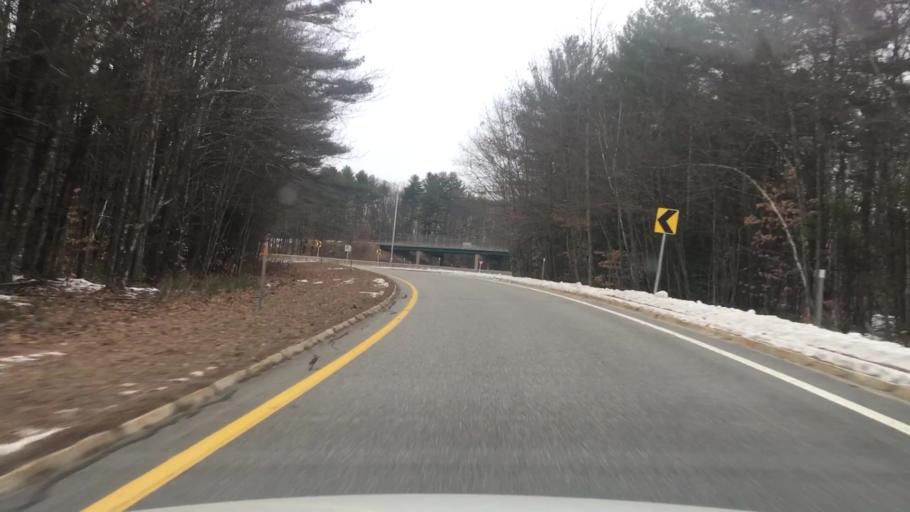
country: US
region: New Hampshire
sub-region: Merrimack County
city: Hopkinton
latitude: 43.1826
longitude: -71.6520
